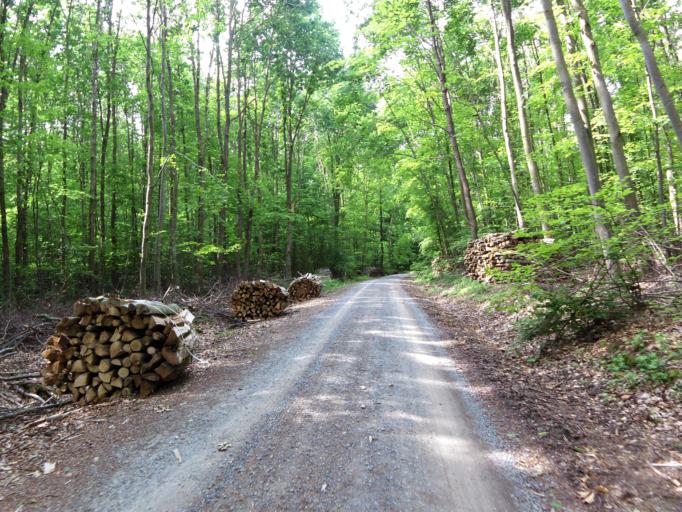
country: DE
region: Bavaria
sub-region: Regierungsbezirk Unterfranken
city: Wuerzburg
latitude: 49.7606
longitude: 9.8574
